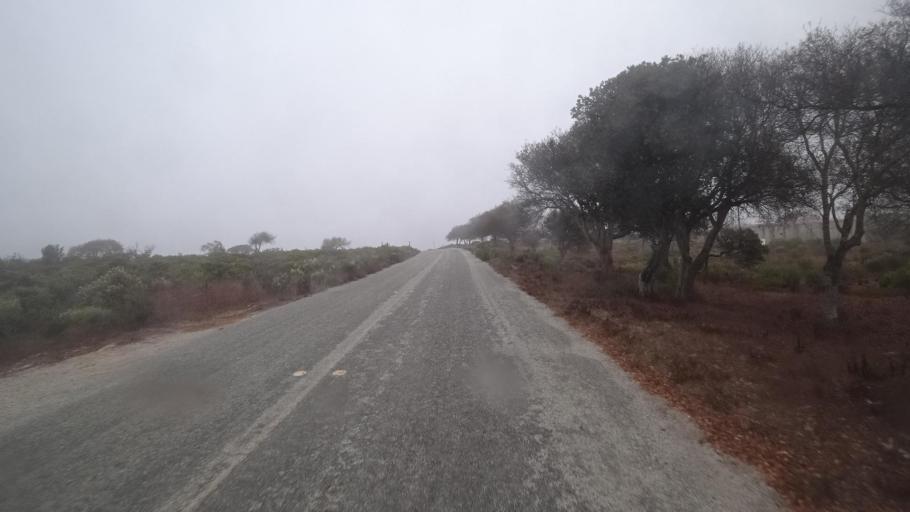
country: US
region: California
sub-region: Monterey County
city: Marina
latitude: 36.6364
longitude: -121.7355
